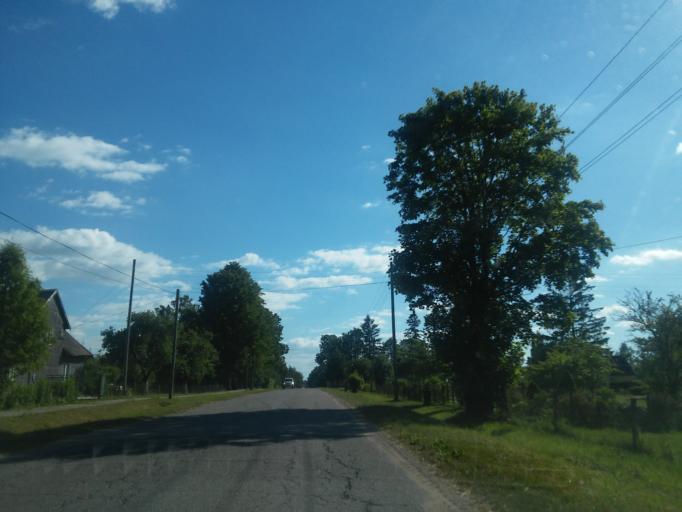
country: LV
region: Vainode
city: Vainode
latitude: 56.4245
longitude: 21.8633
